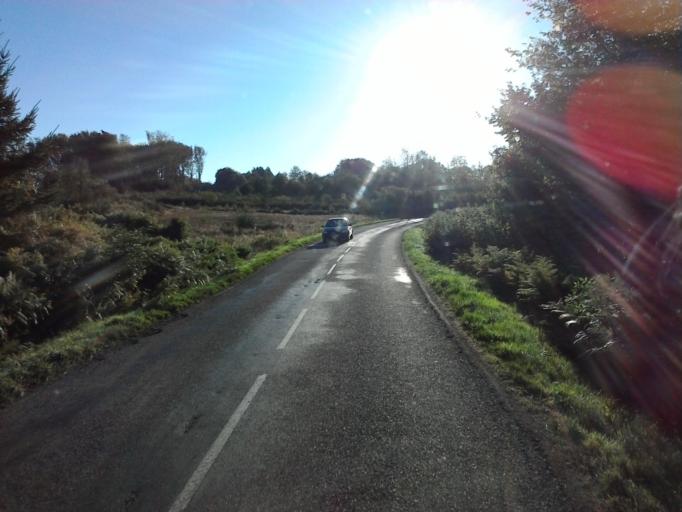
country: FR
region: Bourgogne
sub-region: Departement de la Cote-d'Or
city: Saulieu
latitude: 47.2739
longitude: 4.1064
